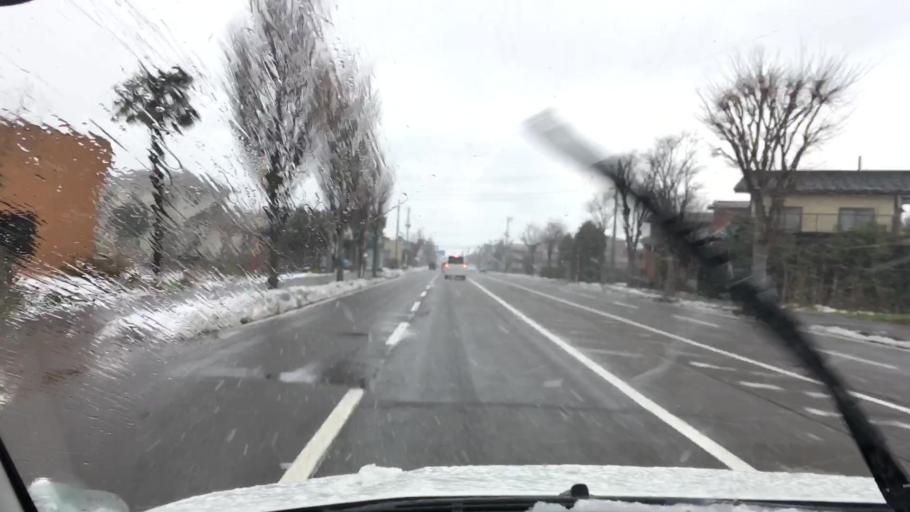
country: JP
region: Niigata
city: Joetsu
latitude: 37.1186
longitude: 138.2328
